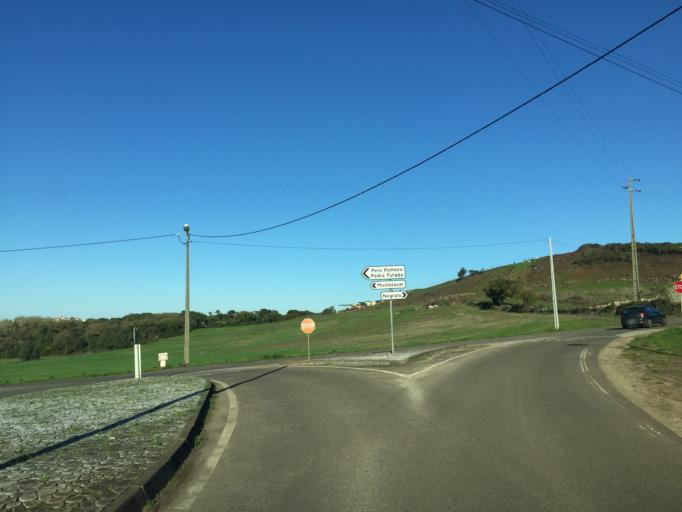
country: PT
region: Lisbon
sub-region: Sintra
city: Almargem
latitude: 38.8704
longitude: -9.2862
